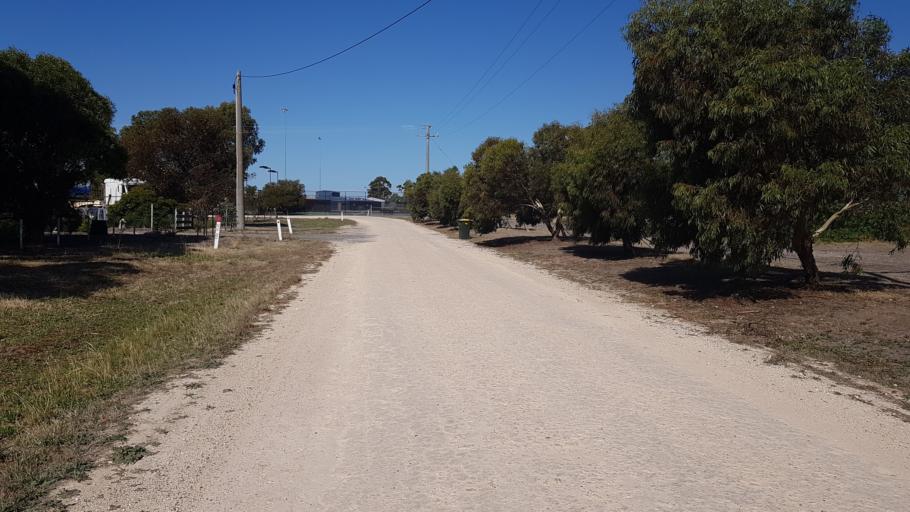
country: AU
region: Victoria
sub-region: Horsham
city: Horsham
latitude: -36.7434
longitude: 141.9463
